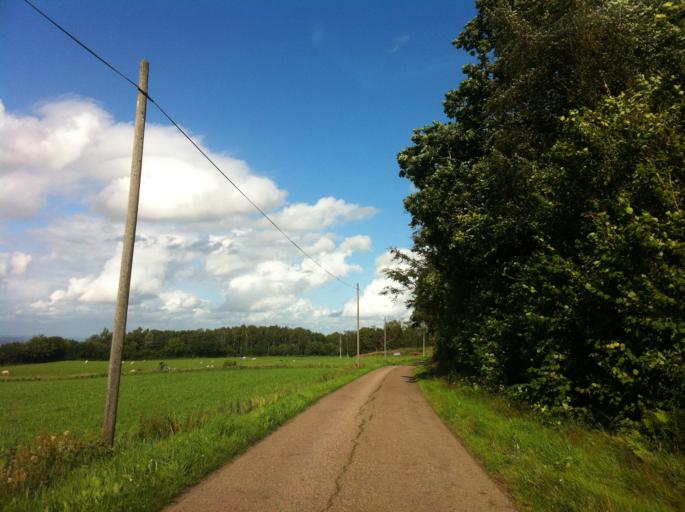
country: SE
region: Skane
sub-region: Bastads Kommun
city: Bastad
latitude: 56.4189
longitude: 12.8961
